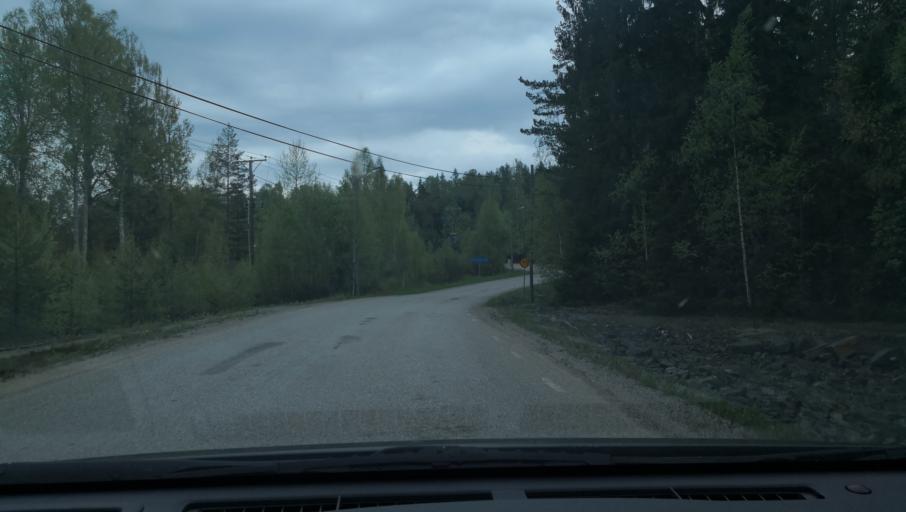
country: SE
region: Vaestmanland
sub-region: Skinnskattebergs Kommun
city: Skinnskatteberg
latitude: 59.8303
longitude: 15.5595
